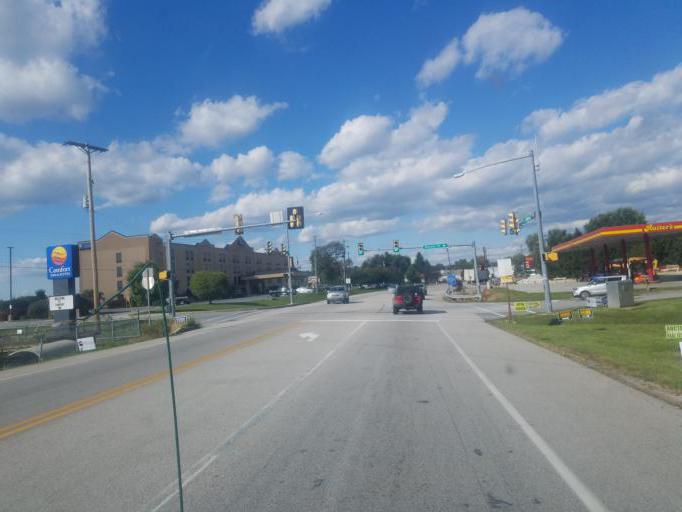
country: US
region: Pennsylvania
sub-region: York County
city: North York
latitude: 39.9952
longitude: -76.7341
